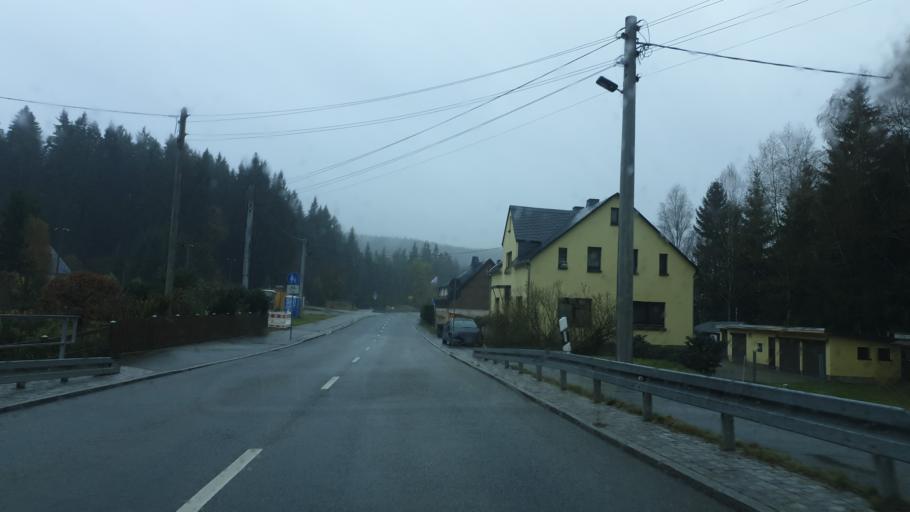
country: DE
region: Saxony
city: Muldenhammer
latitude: 50.4542
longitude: 12.4802
